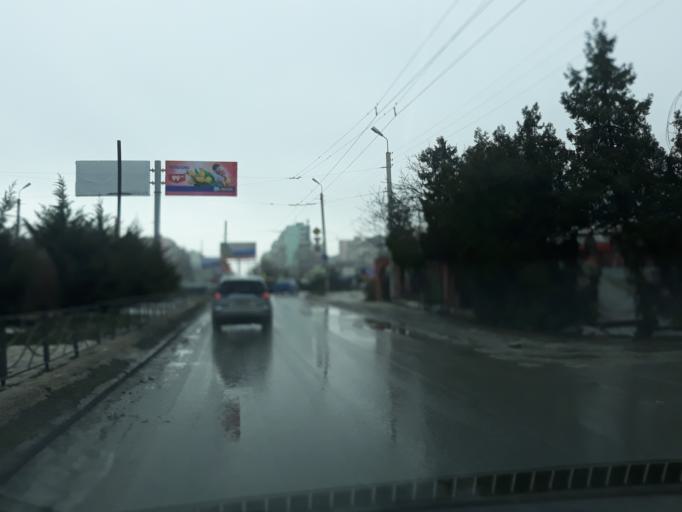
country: RU
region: Rostov
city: Taganrog
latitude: 47.2199
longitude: 38.8629
